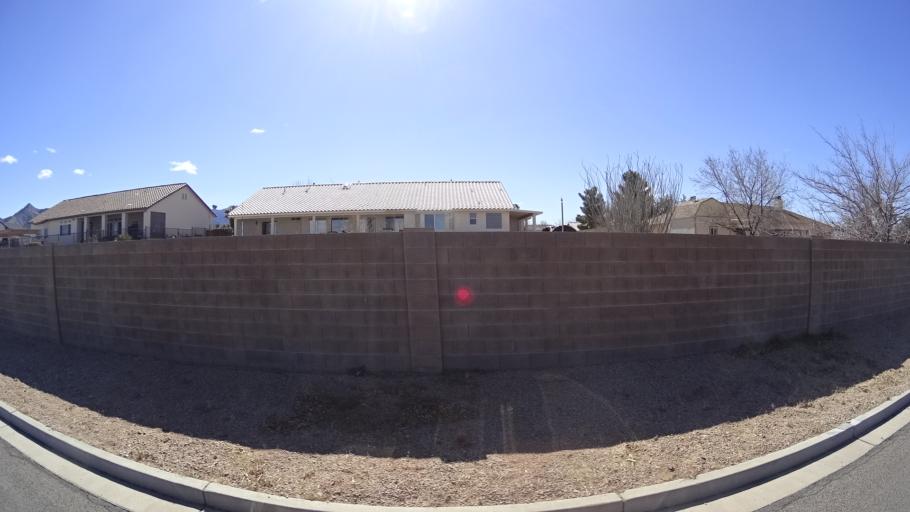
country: US
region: Arizona
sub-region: Mohave County
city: Kingman
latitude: 35.1958
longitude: -113.9786
